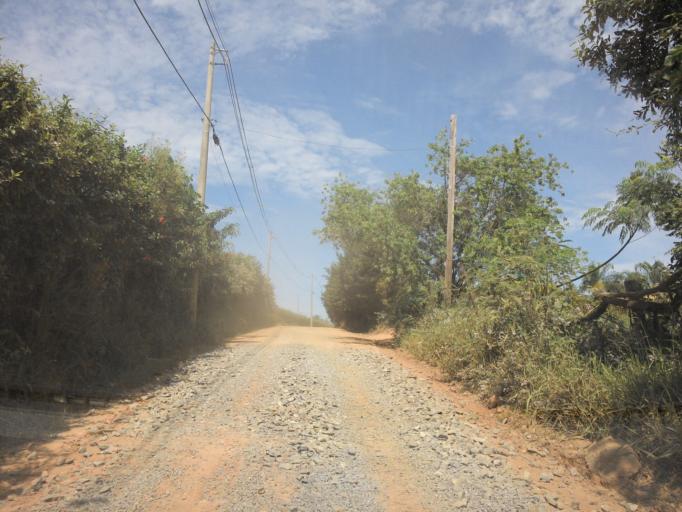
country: BR
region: Sao Paulo
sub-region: Valinhos
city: Valinhos
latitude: -22.9319
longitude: -46.9880
